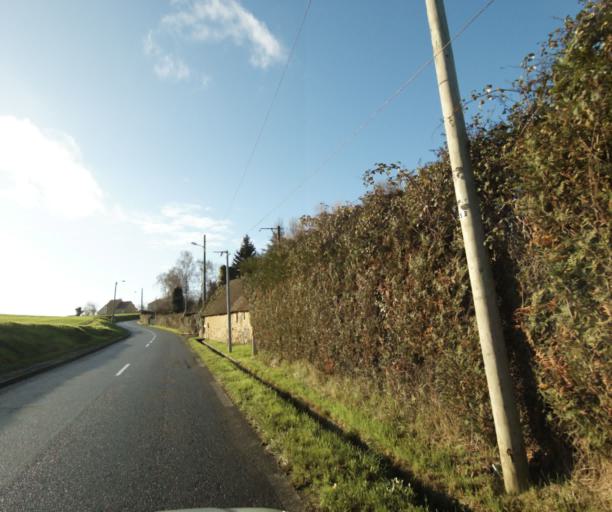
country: FR
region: Pays de la Loire
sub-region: Departement de la Sarthe
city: Coulaines
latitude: 48.0247
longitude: 0.2194
